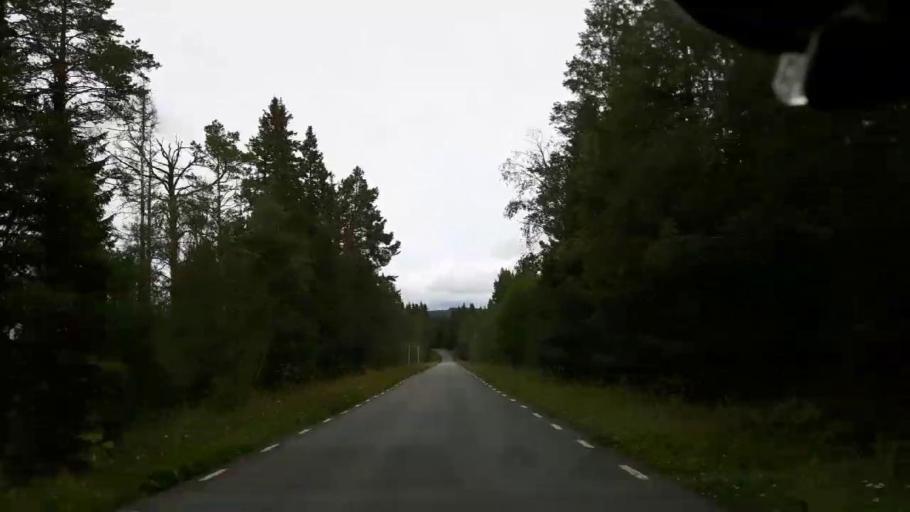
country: SE
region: Jaemtland
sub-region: Krokoms Kommun
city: Valla
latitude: 63.4627
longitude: 14.0632
